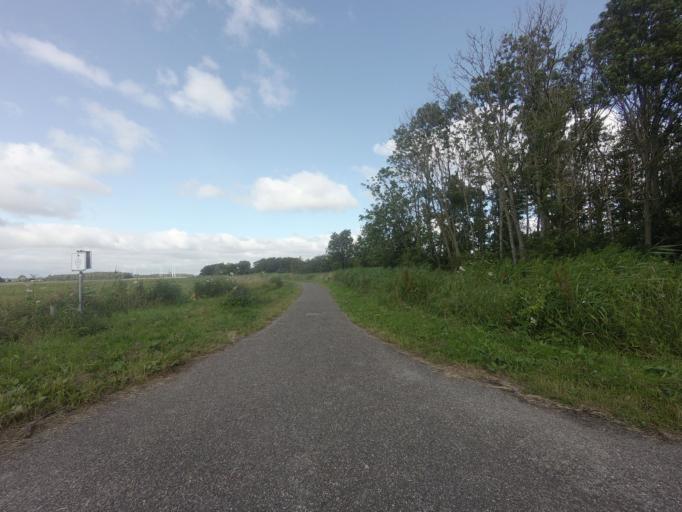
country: NL
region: North Holland
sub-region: Gemeente Haarlem
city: Haarlem
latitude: 52.3916
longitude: 4.6968
